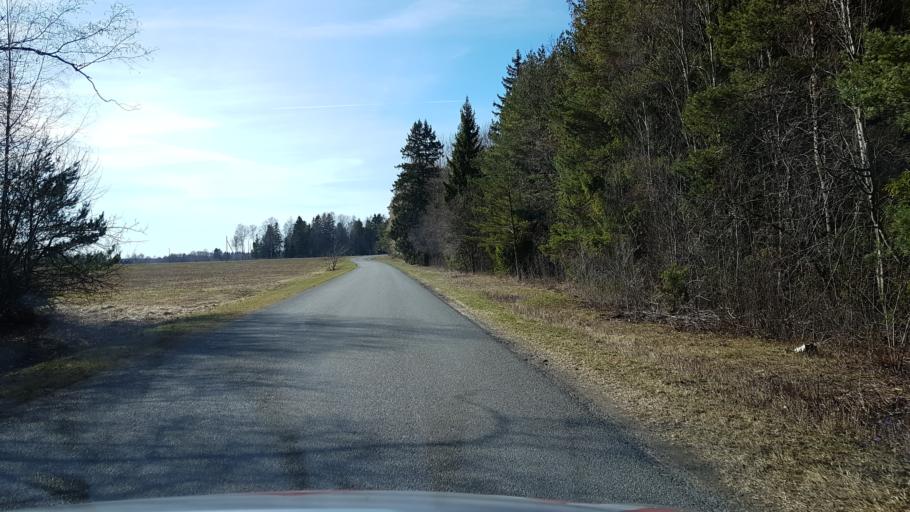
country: EE
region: Harju
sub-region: Nissi vald
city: Riisipere
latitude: 59.0987
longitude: 24.3292
